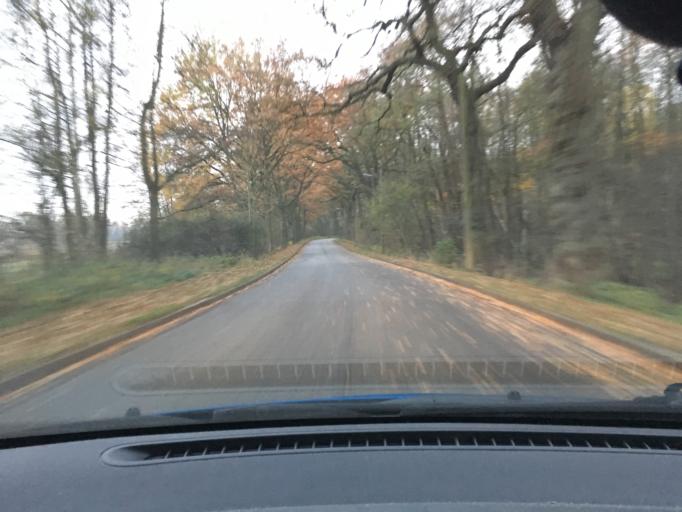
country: DE
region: Lower Saxony
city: Winsen
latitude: 53.4061
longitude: 10.2076
